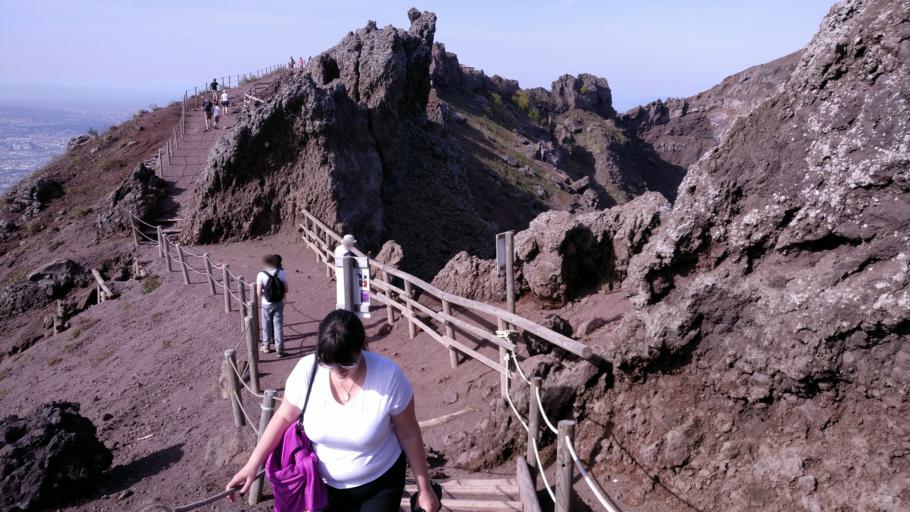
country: IT
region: Campania
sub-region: Provincia di Napoli
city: Torre del Greco
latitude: 40.8190
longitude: 14.4249
